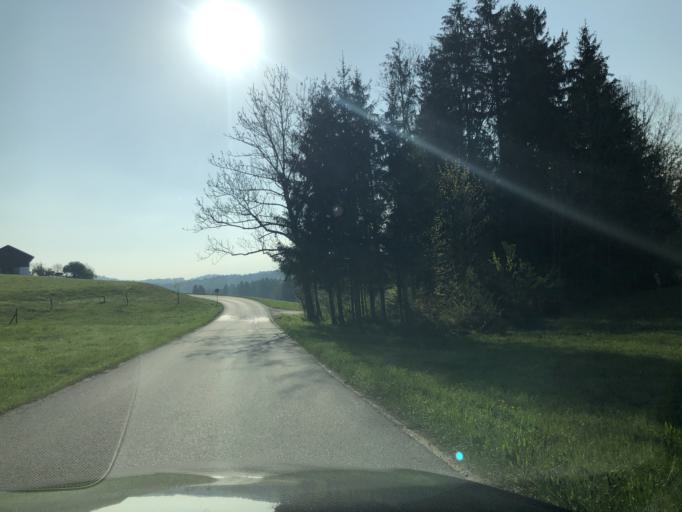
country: DE
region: Bavaria
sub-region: Upper Bavaria
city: Frasdorf
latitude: 47.8107
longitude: 12.2424
